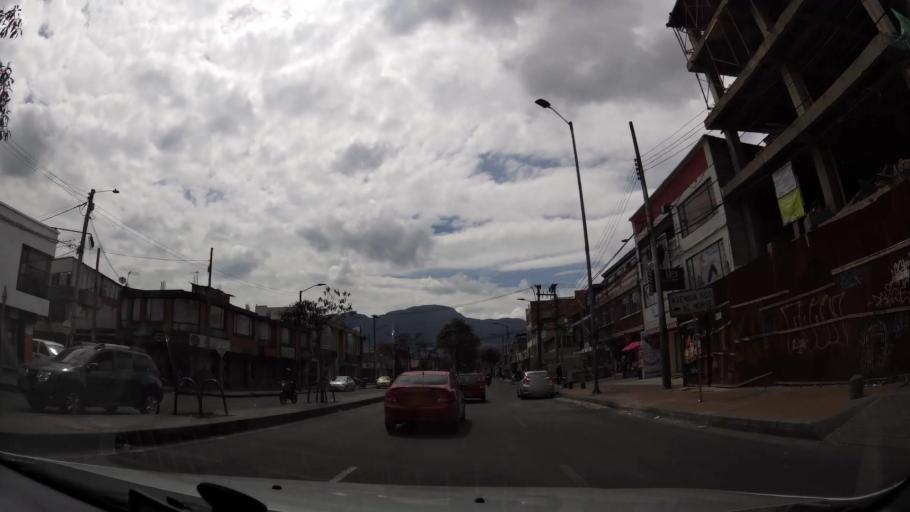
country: CO
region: Bogota D.C.
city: Bogota
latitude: 4.6029
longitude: -74.1000
